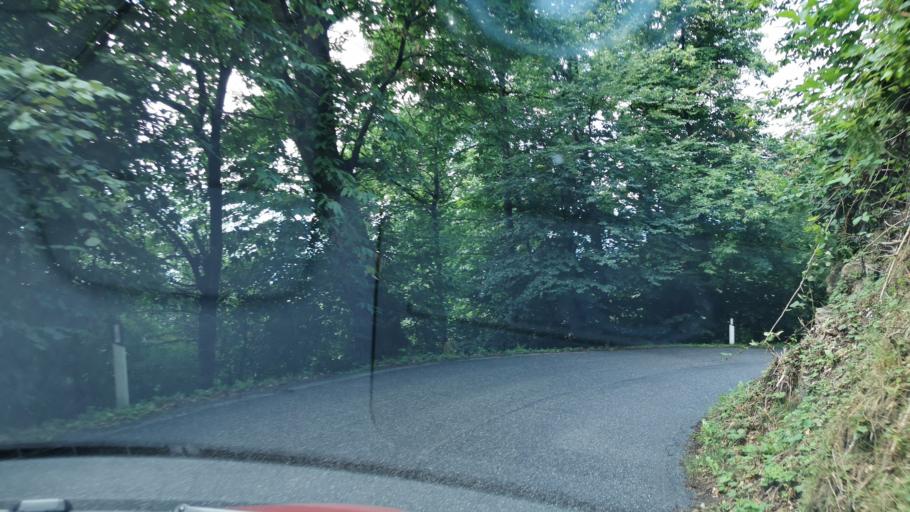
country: IT
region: Lombardy
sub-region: Provincia di Lecco
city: Moggio
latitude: 45.9206
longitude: 9.4893
